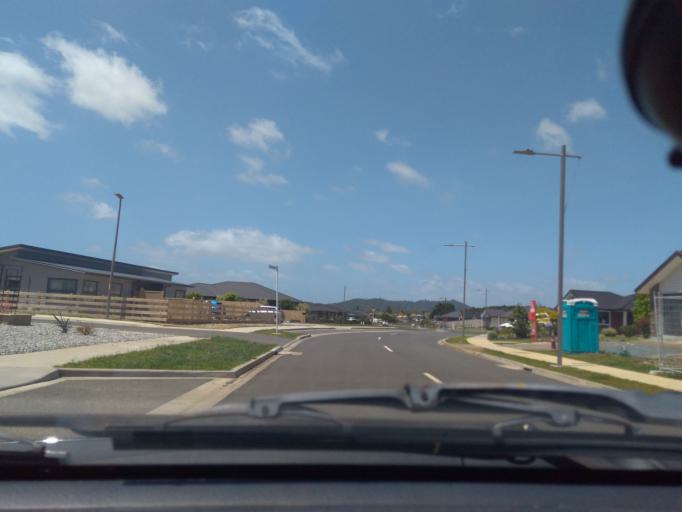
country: NZ
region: Northland
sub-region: Whangarei
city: Whangarei
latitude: -35.6741
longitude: 174.3165
